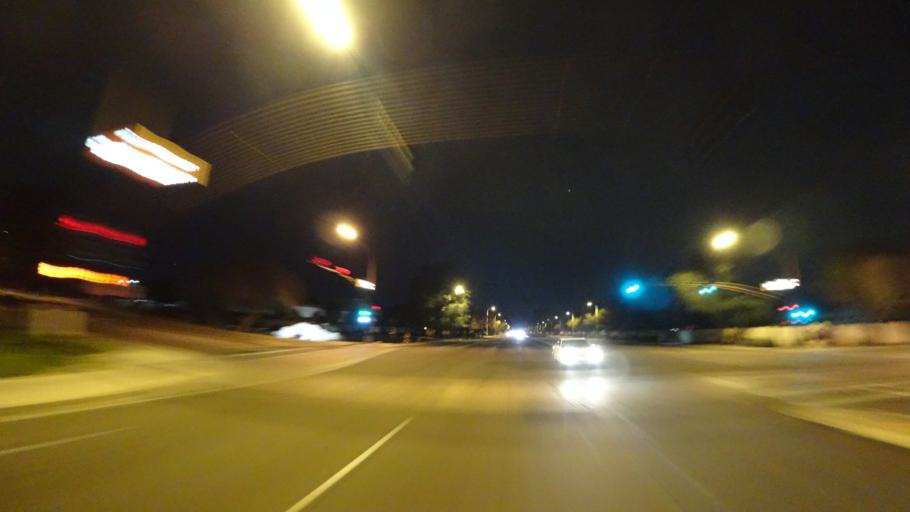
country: US
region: Arizona
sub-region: Maricopa County
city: Chandler
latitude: 33.3063
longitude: -111.8111
